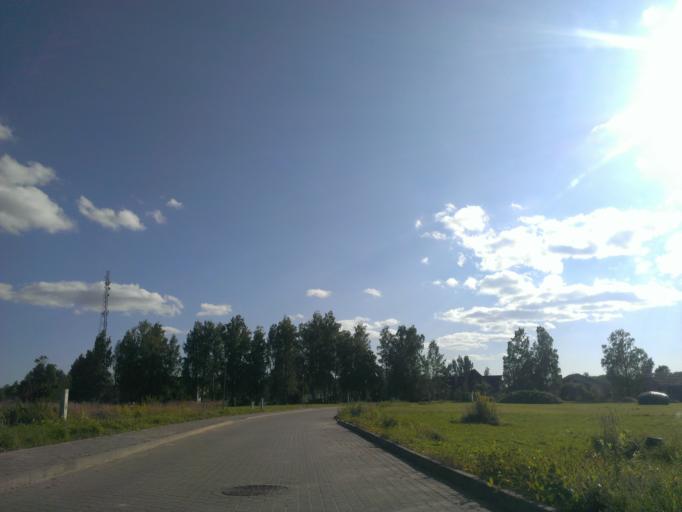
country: LV
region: Sigulda
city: Sigulda
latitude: 57.1662
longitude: 24.8773
